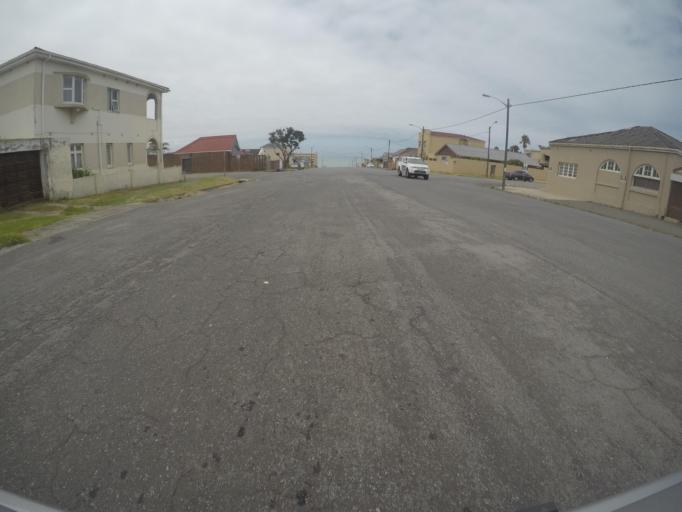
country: ZA
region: Eastern Cape
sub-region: Buffalo City Metropolitan Municipality
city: East London
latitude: -33.0143
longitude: 27.9168
